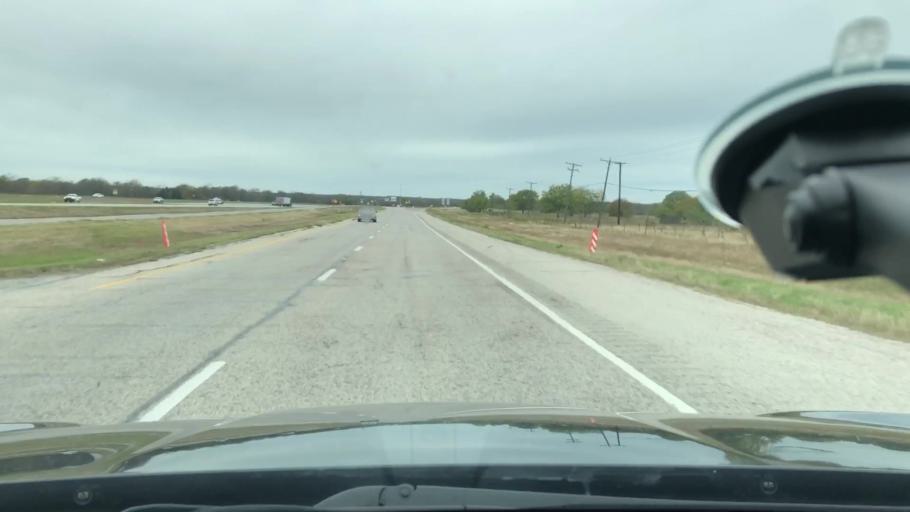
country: US
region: Texas
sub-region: Kaufman County
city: Talty
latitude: 32.7406
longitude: -96.3644
